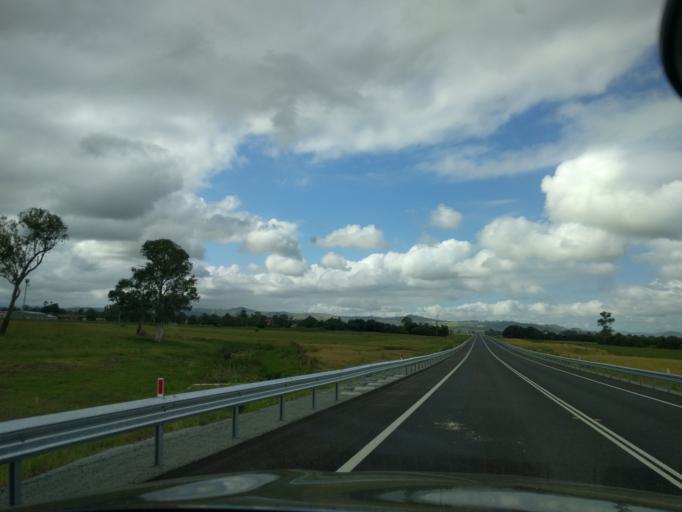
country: AU
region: Queensland
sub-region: Logan
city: Cedar Vale
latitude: -27.9808
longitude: 152.9917
